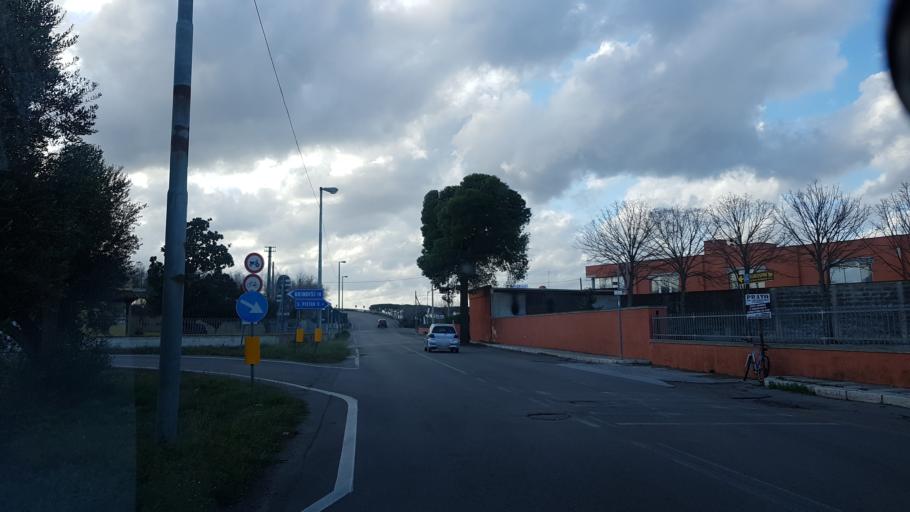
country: IT
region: Apulia
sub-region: Provincia di Brindisi
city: Torchiarolo
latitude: 40.4866
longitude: 18.0441
